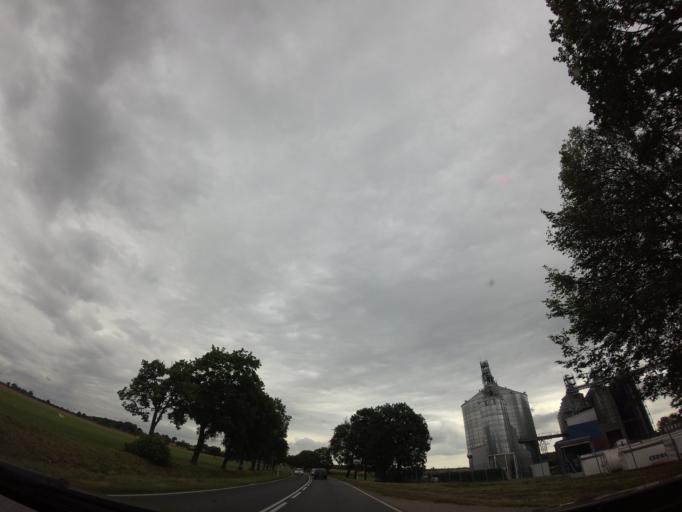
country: PL
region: Masovian Voivodeship
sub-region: Powiat ciechanowski
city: Ojrzen
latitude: 52.8410
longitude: 20.5069
